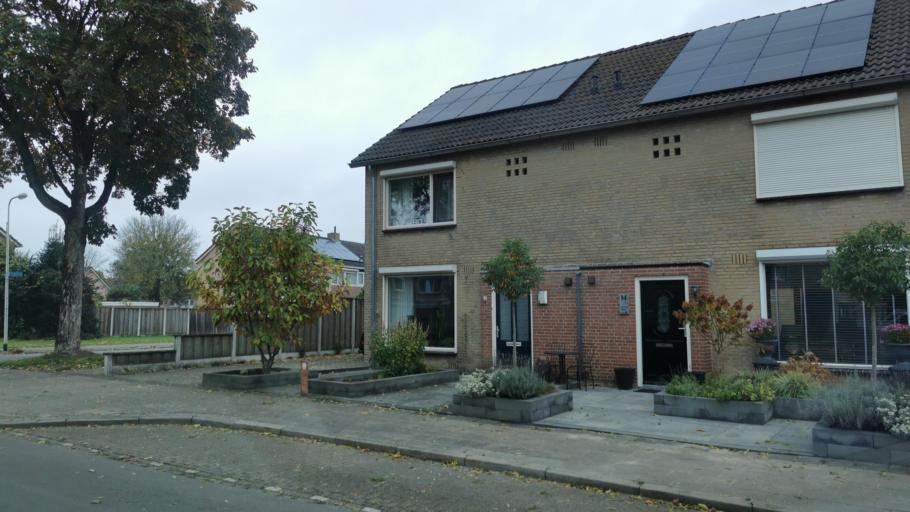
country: NL
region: Overijssel
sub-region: Gemeente Losser
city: Losser
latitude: 52.2523
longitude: 7.0084
